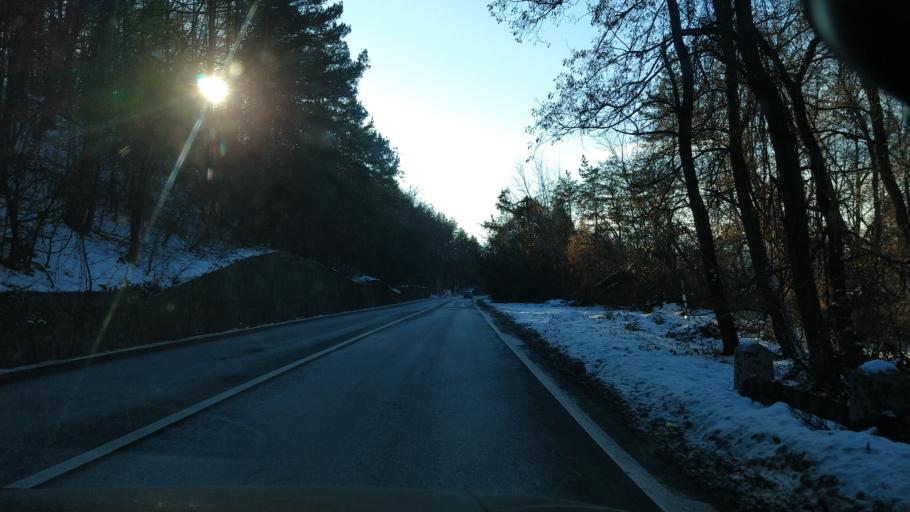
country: RO
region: Bacau
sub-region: Comuna Luizi-Calugara
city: Luizi-Calugara
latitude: 46.4934
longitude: 26.7932
